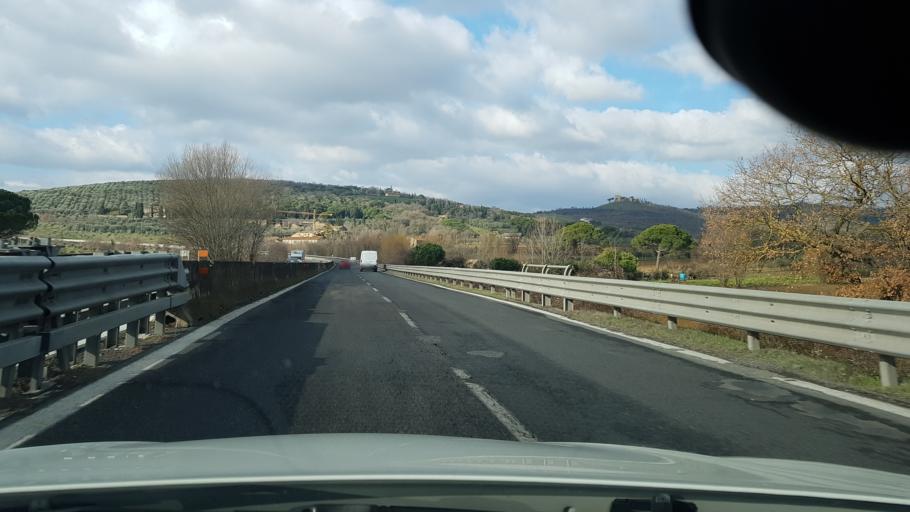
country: IT
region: Umbria
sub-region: Provincia di Perugia
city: Tuoro sul Trasimeno
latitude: 43.1958
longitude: 12.0601
